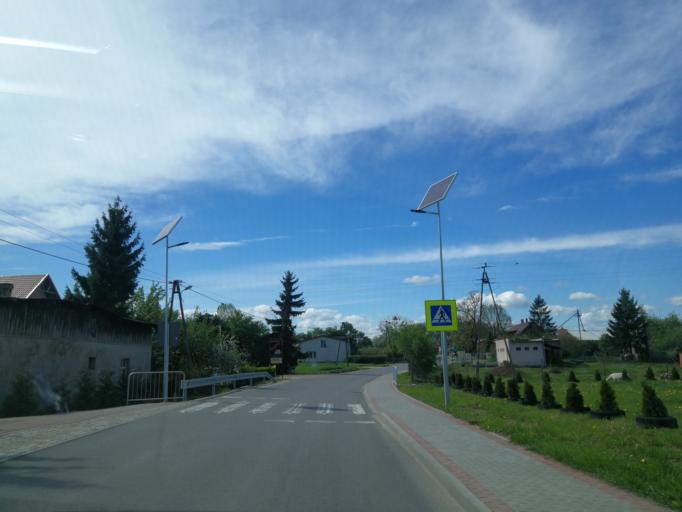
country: PL
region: Warmian-Masurian Voivodeship
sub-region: Powiat ilawski
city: Lubawa
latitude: 53.5989
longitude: 19.6963
